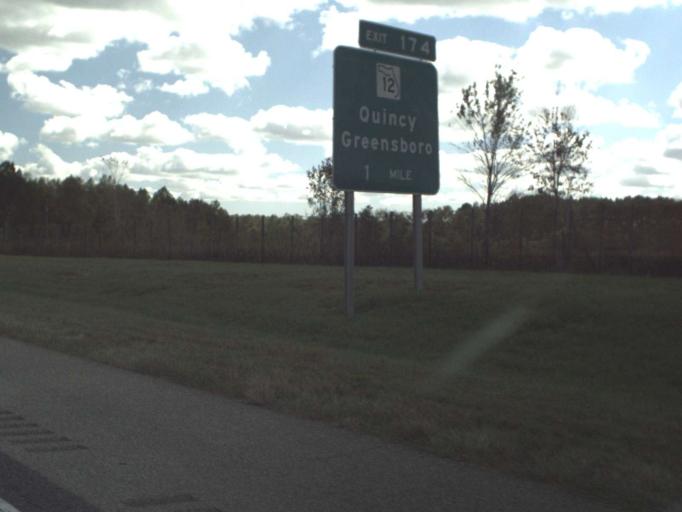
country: US
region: Florida
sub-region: Gadsden County
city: Gretna
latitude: 30.5882
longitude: -84.7179
